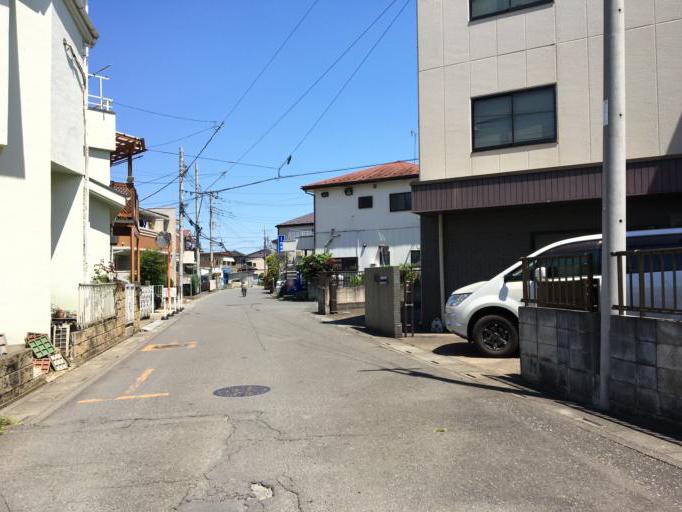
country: JP
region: Saitama
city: Sakado
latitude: 35.9514
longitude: 139.3853
